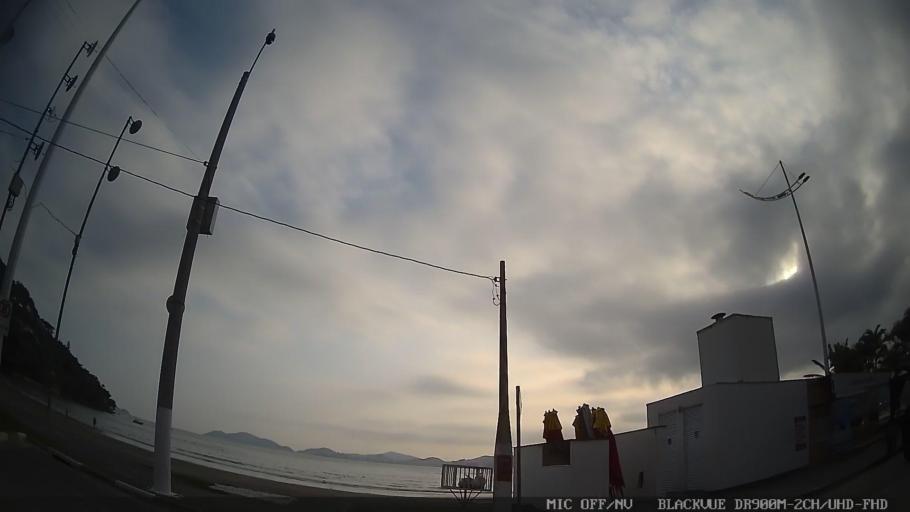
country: BR
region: Sao Paulo
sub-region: Guaruja
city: Guaruja
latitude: -23.9926
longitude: -46.2018
